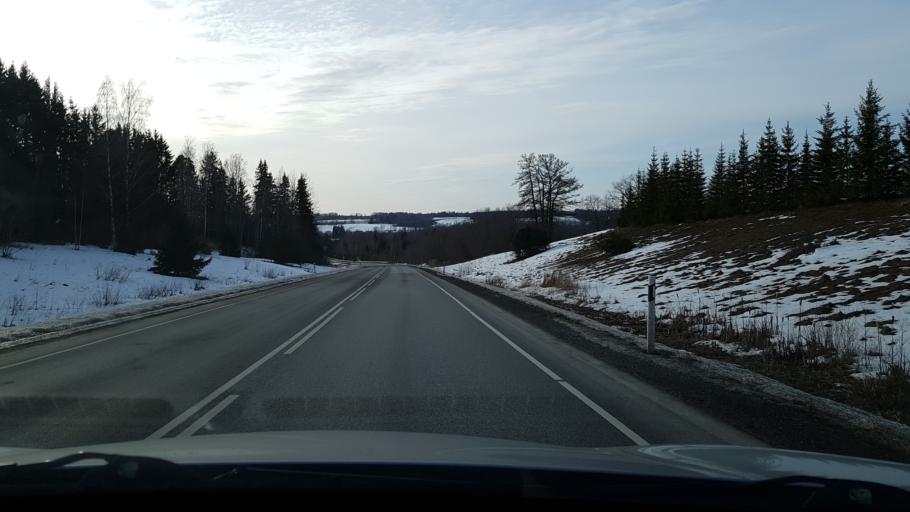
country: EE
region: Viljandimaa
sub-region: Viljandi linn
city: Viljandi
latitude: 58.3430
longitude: 25.4918
